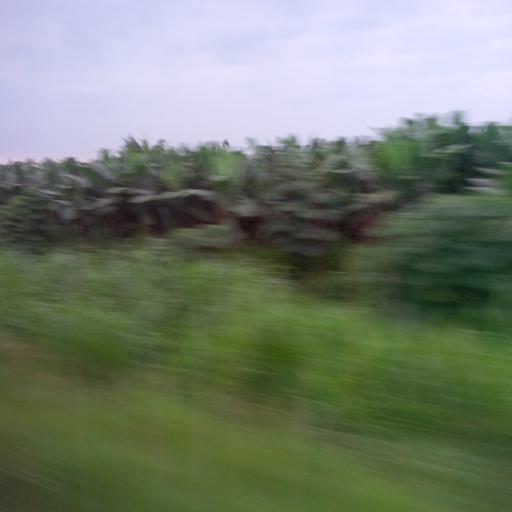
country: EC
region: Canar
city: La Troncal
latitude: -2.3277
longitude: -79.3313
